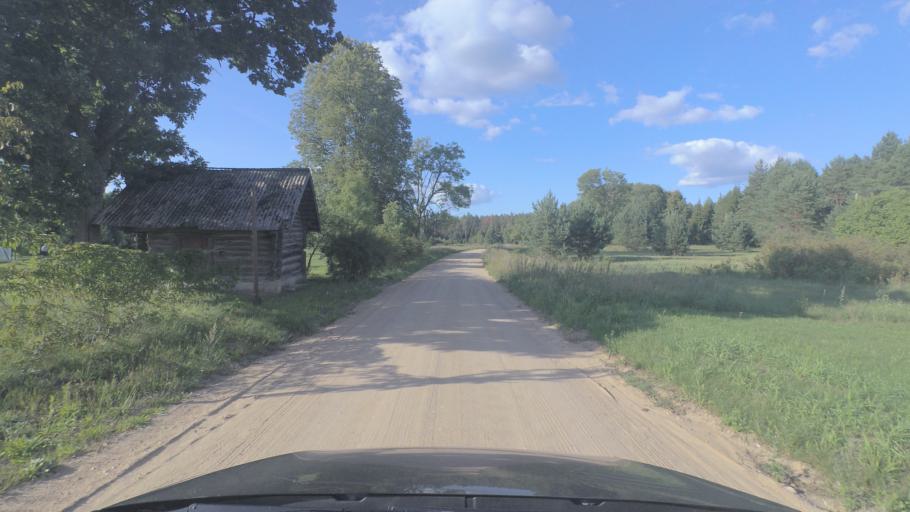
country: LT
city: Pabrade
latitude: 55.1408
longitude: 25.7369
